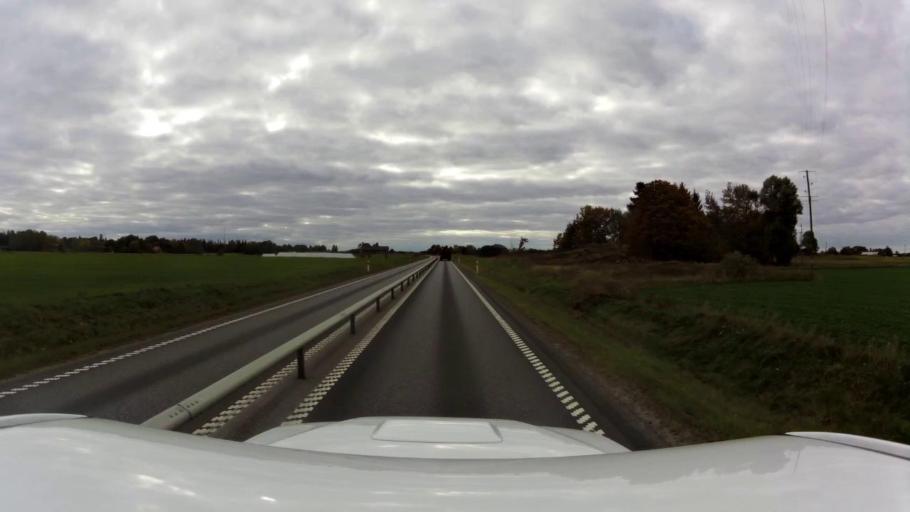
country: SE
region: OEstergoetland
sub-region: Linkopings Kommun
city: Malmslatt
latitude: 58.3417
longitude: 15.5539
